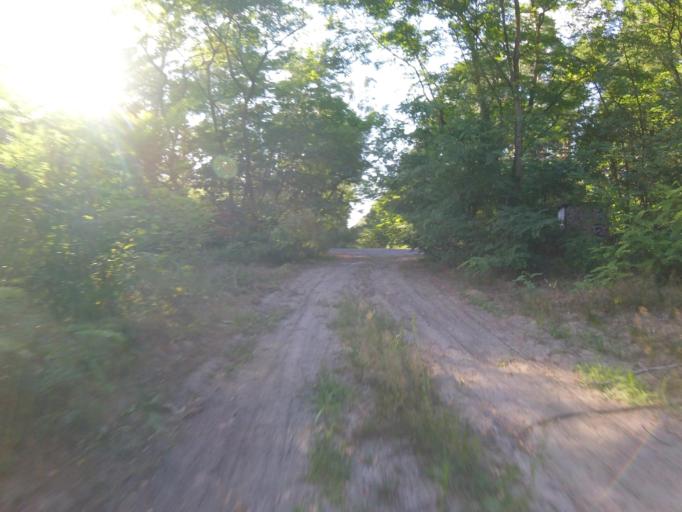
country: DE
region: Berlin
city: Schmockwitz
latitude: 52.3280
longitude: 13.7251
